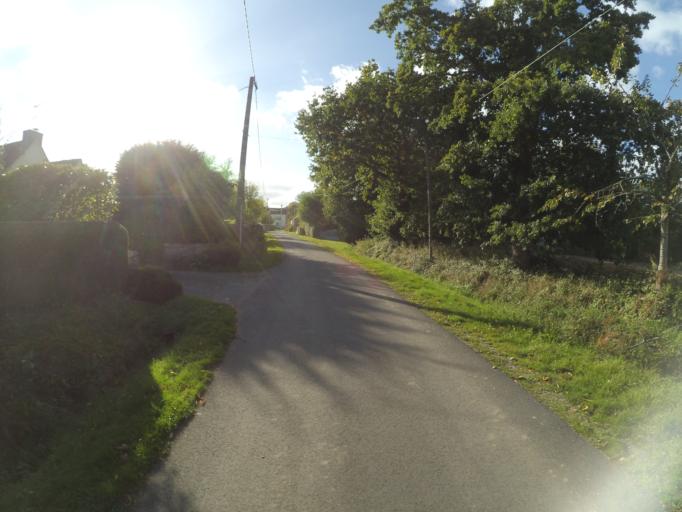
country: FR
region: Brittany
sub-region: Departement du Morbihan
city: Peillac
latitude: 47.7207
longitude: -2.2220
